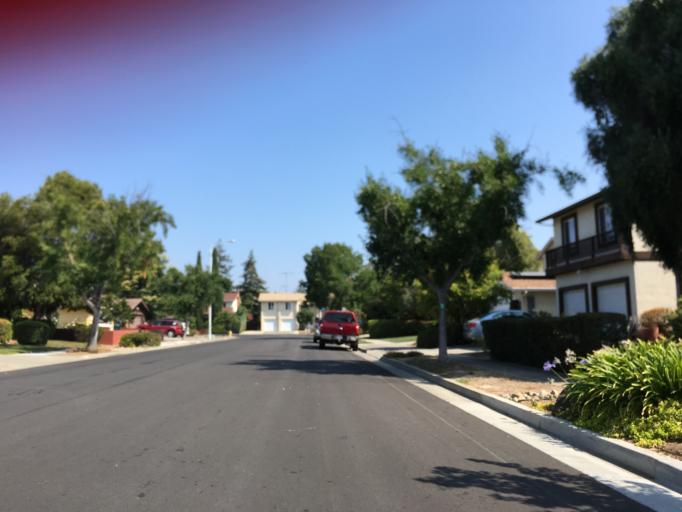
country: US
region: California
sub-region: Santa Clara County
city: Cupertino
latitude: 37.3250
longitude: -122.0251
